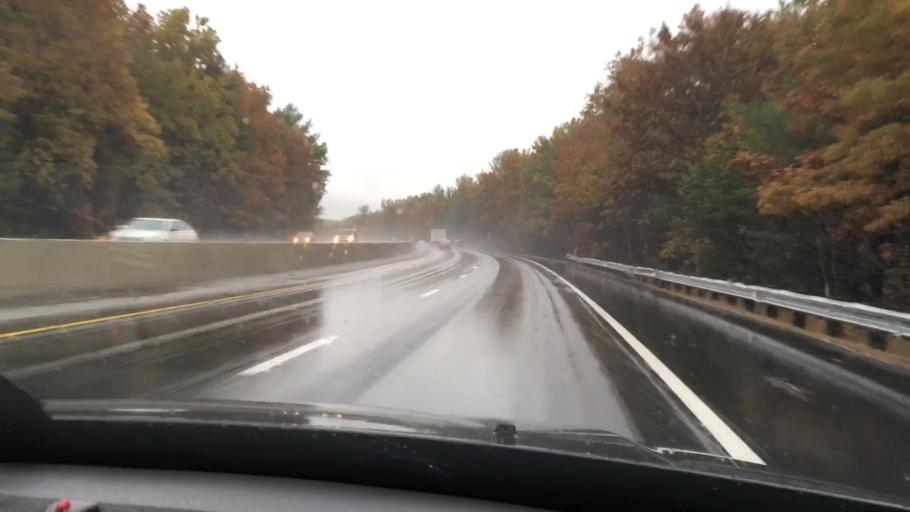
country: US
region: New Hampshire
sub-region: Hillsborough County
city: Pinardville
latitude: 43.0258
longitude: -71.4886
